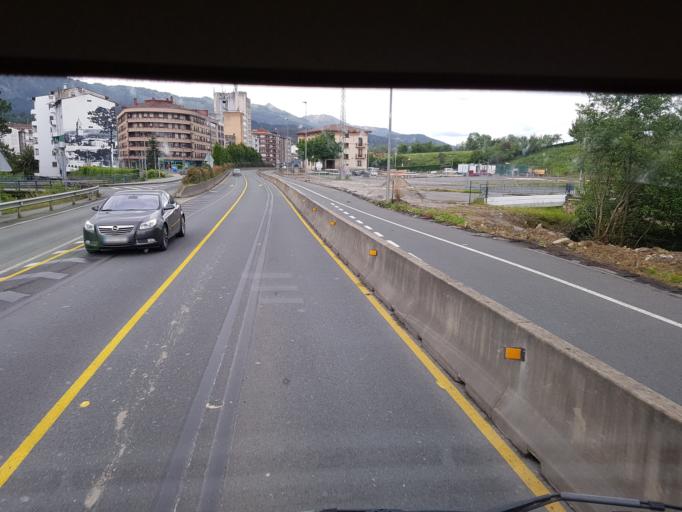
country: ES
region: Basque Country
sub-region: Bizkaia
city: Durango
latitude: 43.1754
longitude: -2.6336
